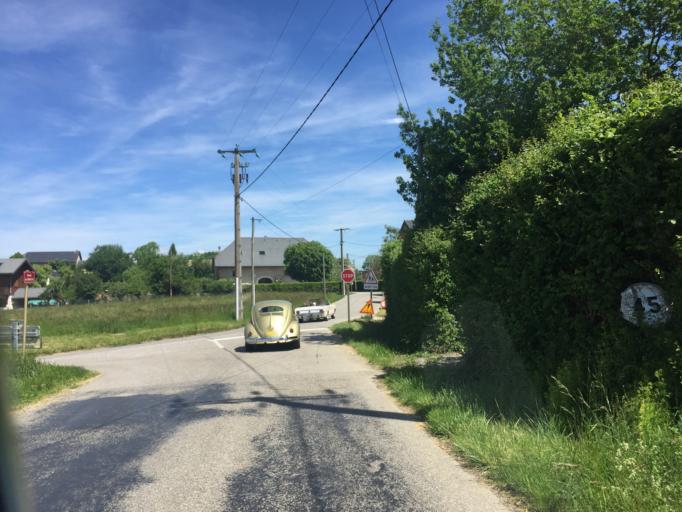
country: FR
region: Rhone-Alpes
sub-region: Departement de la Haute-Savoie
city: Chilly
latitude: 45.9479
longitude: 5.9713
